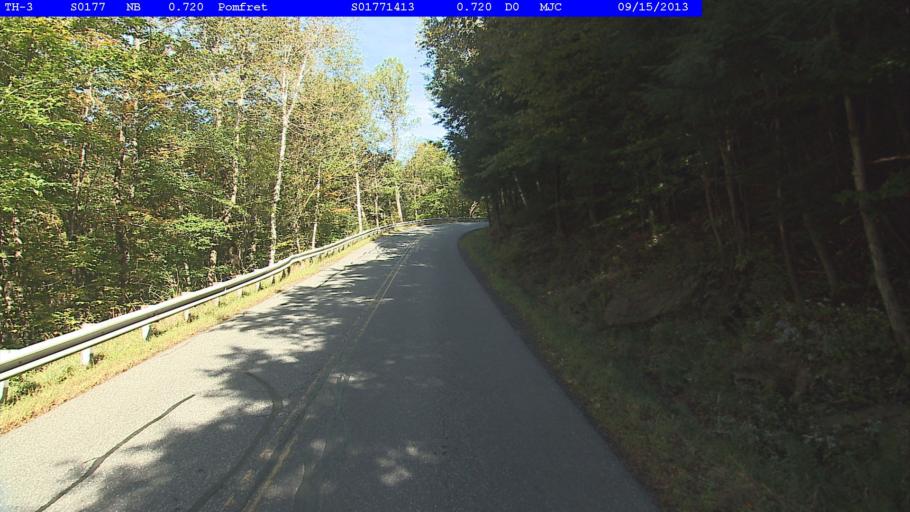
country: US
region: Vermont
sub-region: Windsor County
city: Woodstock
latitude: 43.7331
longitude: -72.4994
